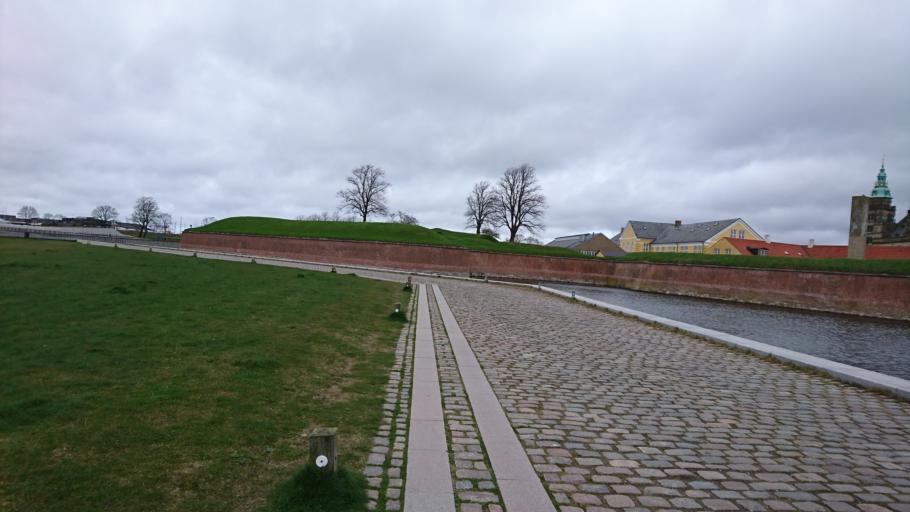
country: DK
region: Capital Region
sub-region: Helsingor Kommune
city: Helsingor
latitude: 56.0374
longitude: 12.6191
